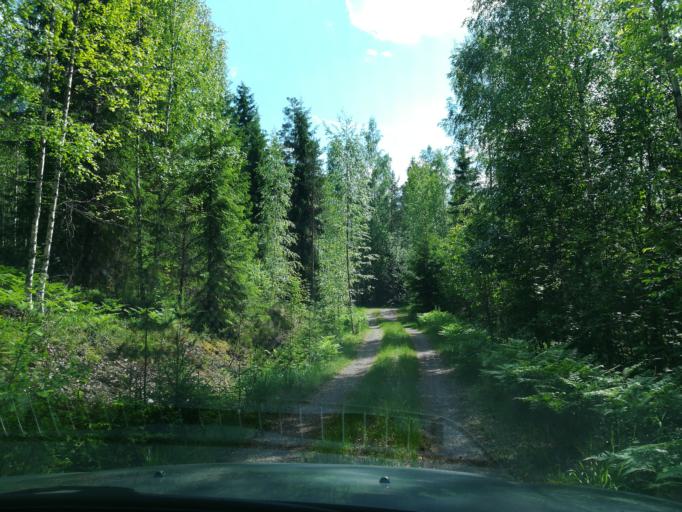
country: FI
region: South Karelia
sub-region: Imatra
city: Ruokolahti
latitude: 61.4824
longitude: 28.8708
